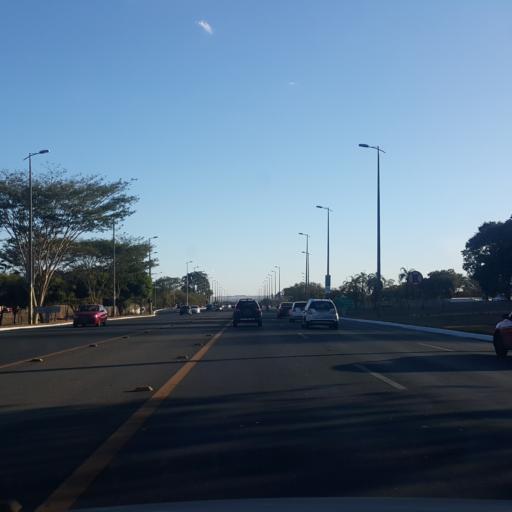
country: BR
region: Federal District
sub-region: Brasilia
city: Brasilia
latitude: -15.8330
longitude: -47.9229
